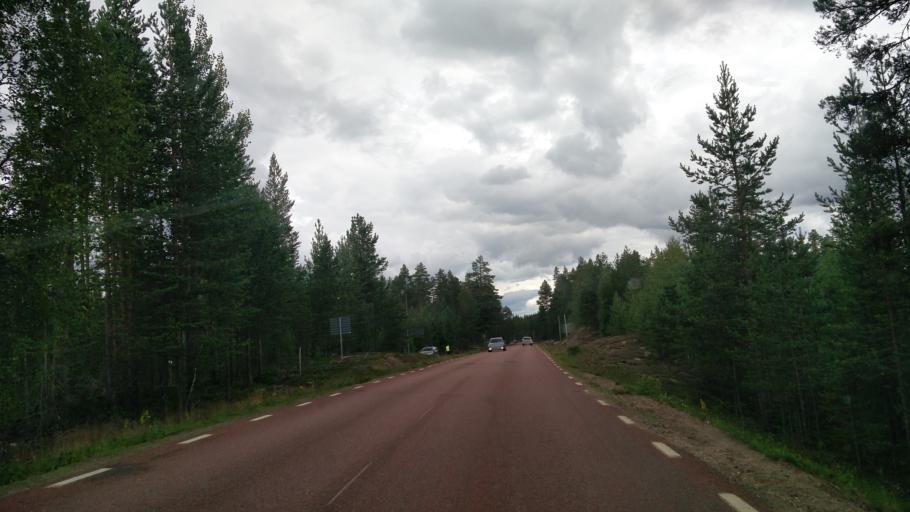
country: NO
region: Hedmark
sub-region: Trysil
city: Innbygda
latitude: 61.1388
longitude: 12.8073
